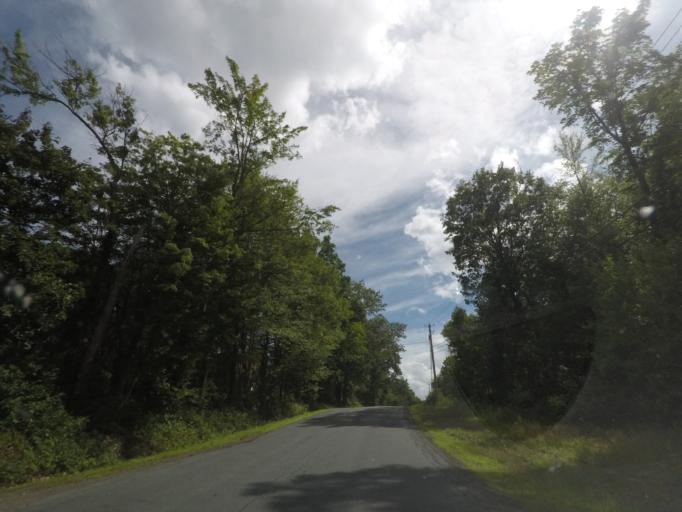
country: US
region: New York
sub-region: Rensselaer County
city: Poestenkill
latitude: 42.6847
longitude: -73.5517
